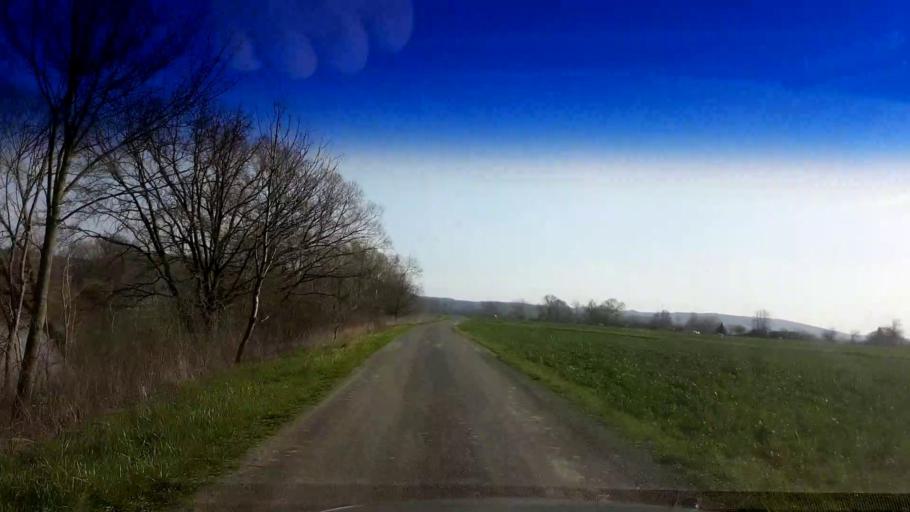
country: DE
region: Bavaria
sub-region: Upper Franconia
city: Ebensfeld
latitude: 50.0485
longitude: 10.9341
